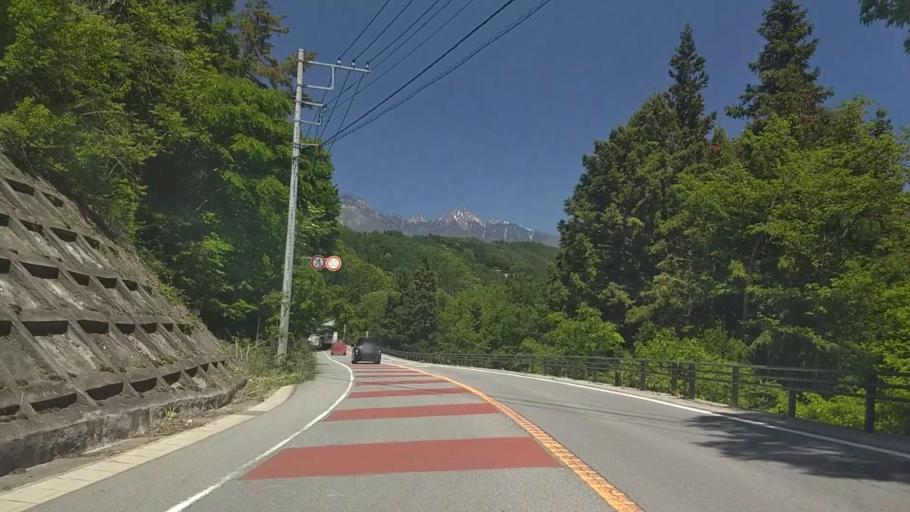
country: JP
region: Yamanashi
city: Nirasaki
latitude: 35.8596
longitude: 138.4302
